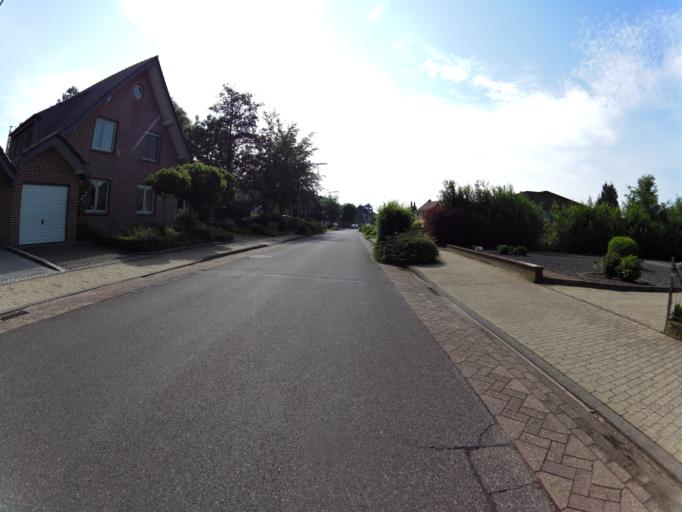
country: DE
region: North Rhine-Westphalia
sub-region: Regierungsbezirk Koln
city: Waldfeucht
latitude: 51.0764
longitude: 5.9940
